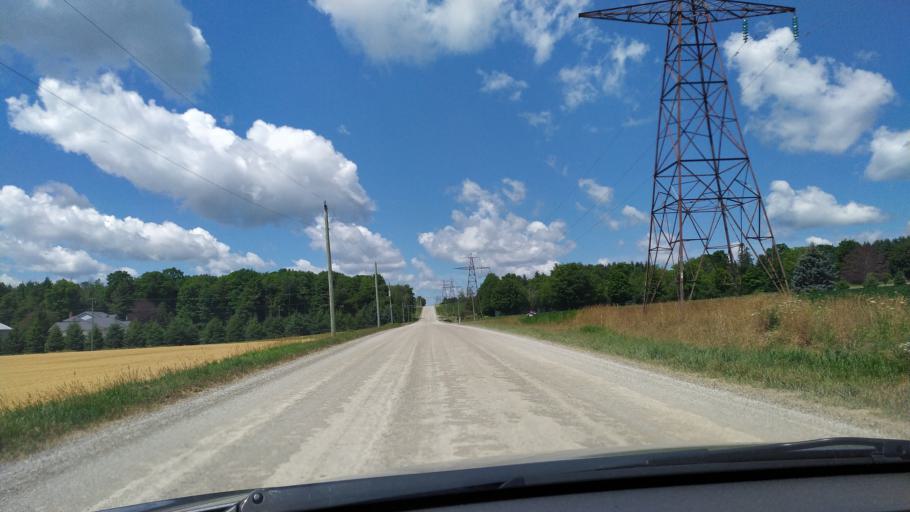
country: CA
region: Ontario
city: Stratford
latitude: 43.3876
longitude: -80.7978
